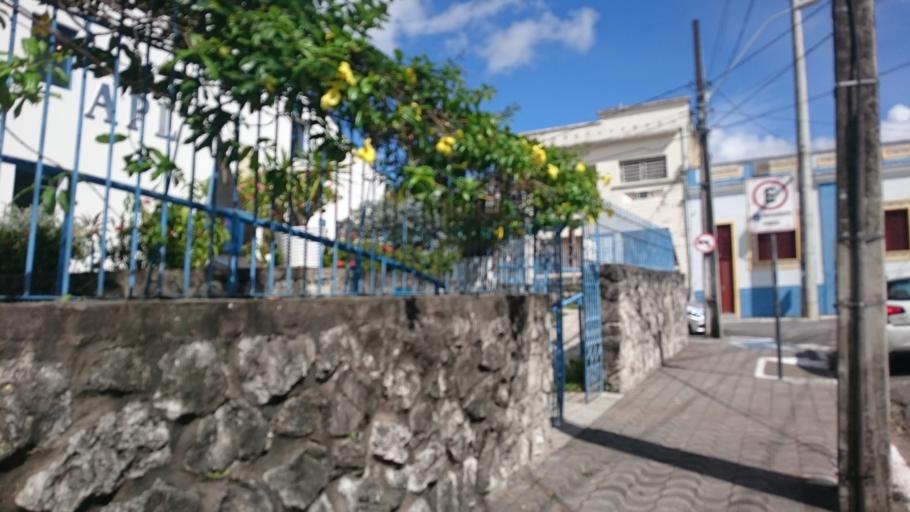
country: BR
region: Paraiba
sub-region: Joao Pessoa
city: Joao Pessoa
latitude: -7.1155
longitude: -34.8832
